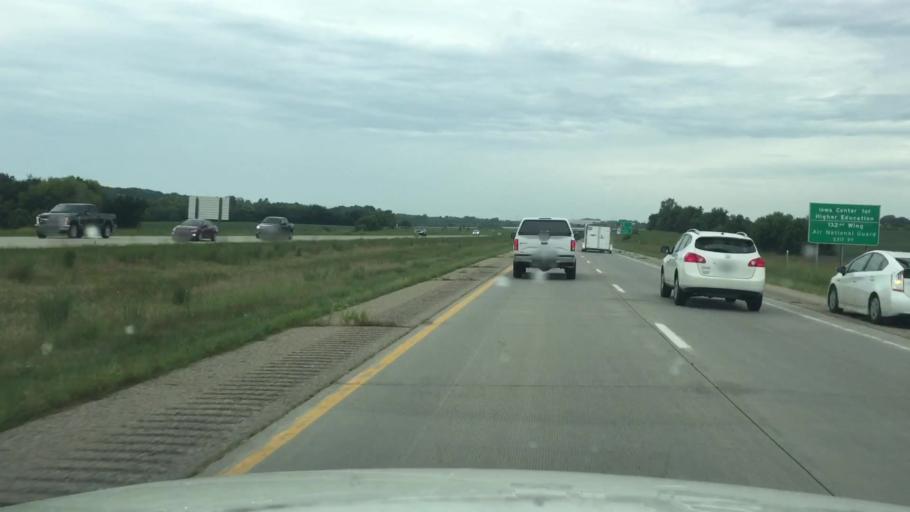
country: US
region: Iowa
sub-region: Warren County
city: Norwalk
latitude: 41.5027
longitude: -93.6344
